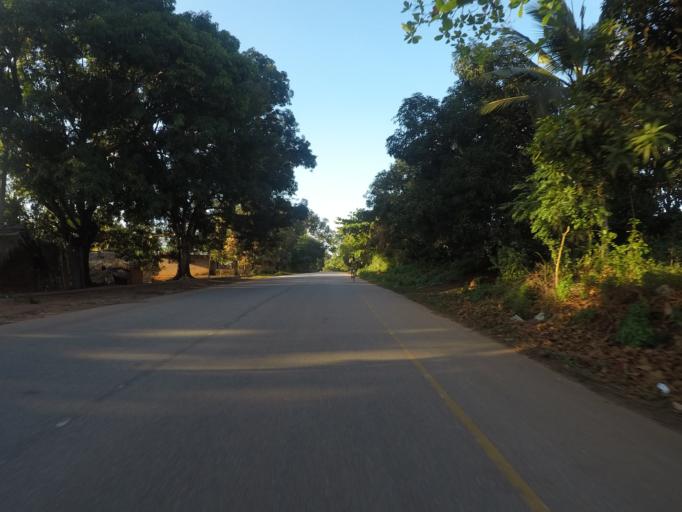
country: TZ
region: Zanzibar North
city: Kijini
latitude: -5.8184
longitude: 39.2916
